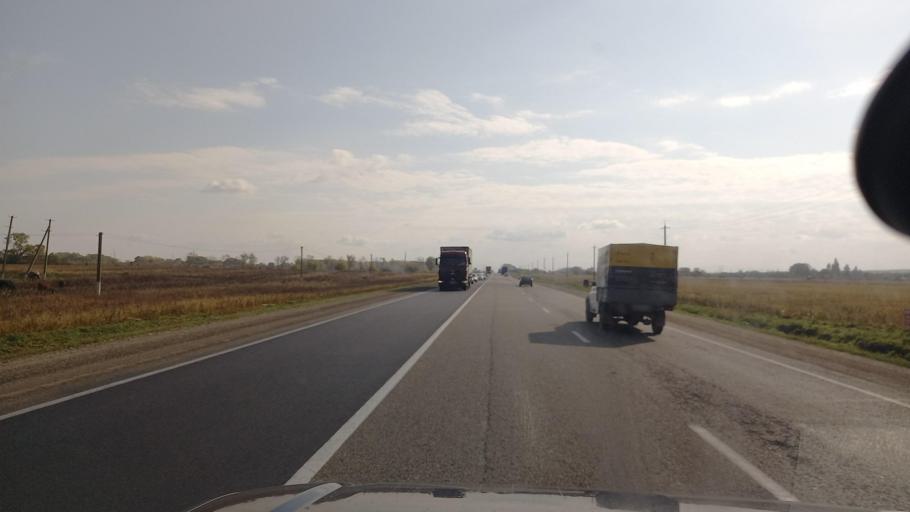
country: RU
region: Krasnodarskiy
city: Novoukrainskiy
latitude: 44.8928
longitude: 38.0663
